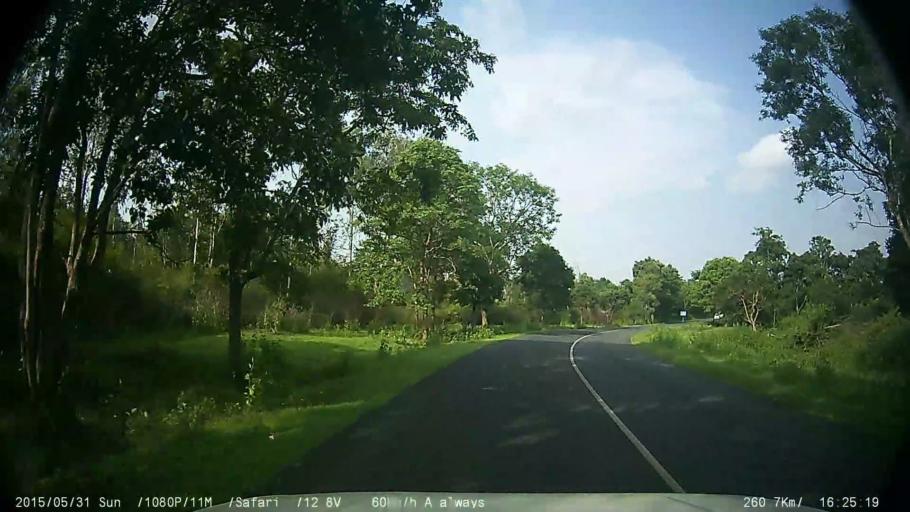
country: IN
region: Karnataka
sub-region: Chamrajnagar
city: Gundlupet
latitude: 11.7658
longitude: 76.5268
